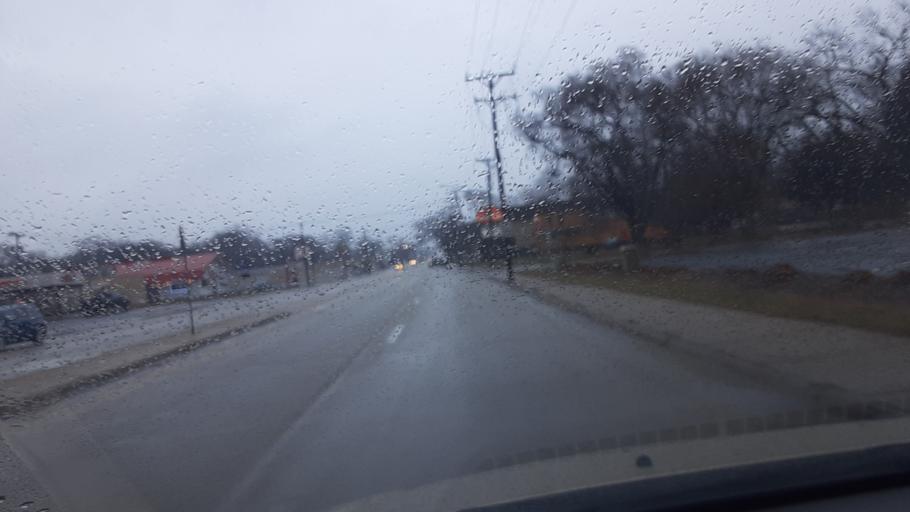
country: US
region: Illinois
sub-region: Winnebago County
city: Rockford
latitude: 42.2883
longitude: -89.1156
